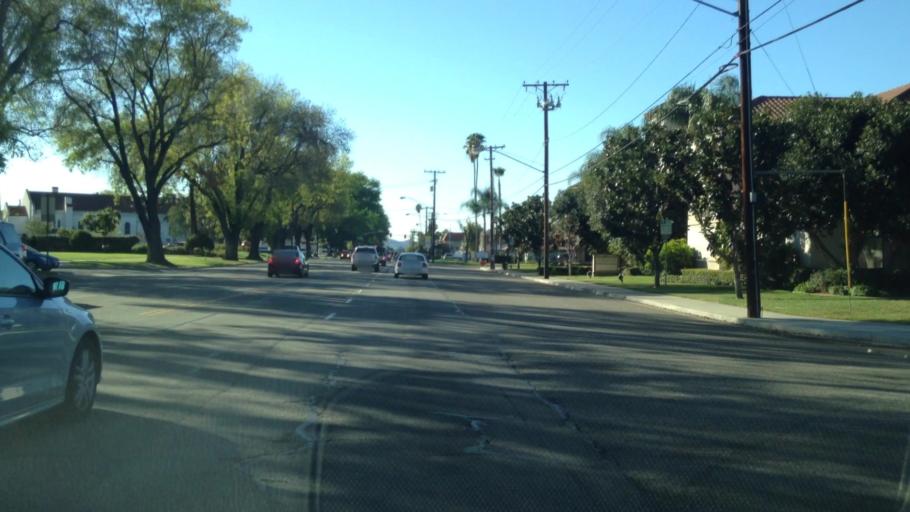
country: US
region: California
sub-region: Riverside County
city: Riverside
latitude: 33.9463
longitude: -117.3937
